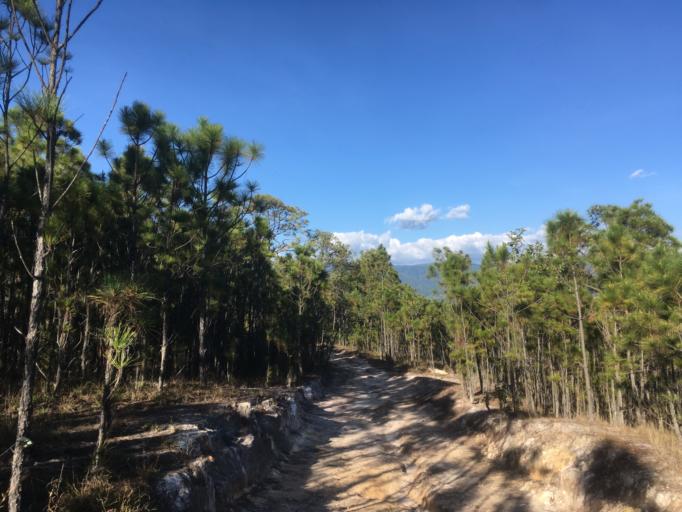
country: MX
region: Michoacan
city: Tzitzio
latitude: 19.6067
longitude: -100.9253
